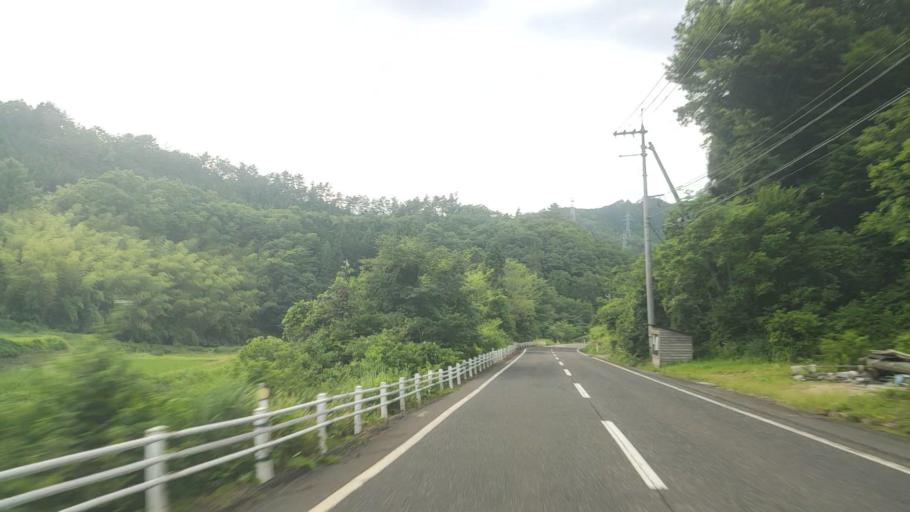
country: JP
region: Tottori
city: Kurayoshi
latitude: 35.2924
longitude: 133.9599
